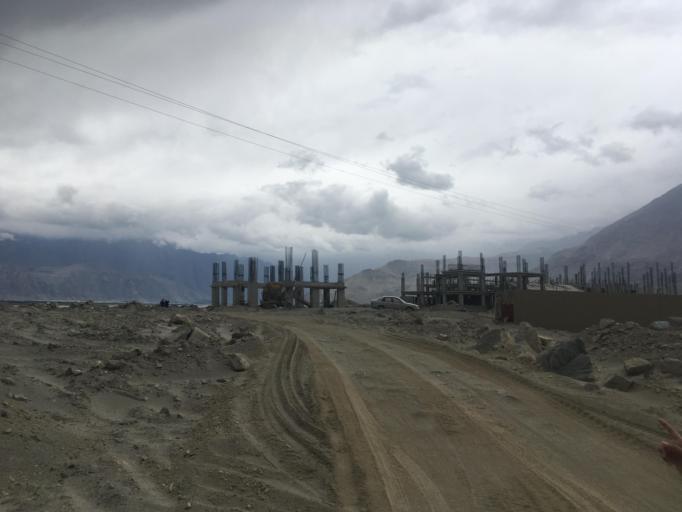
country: PK
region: Gilgit-Baltistan
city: Skardu
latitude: 35.3223
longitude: 75.6558
